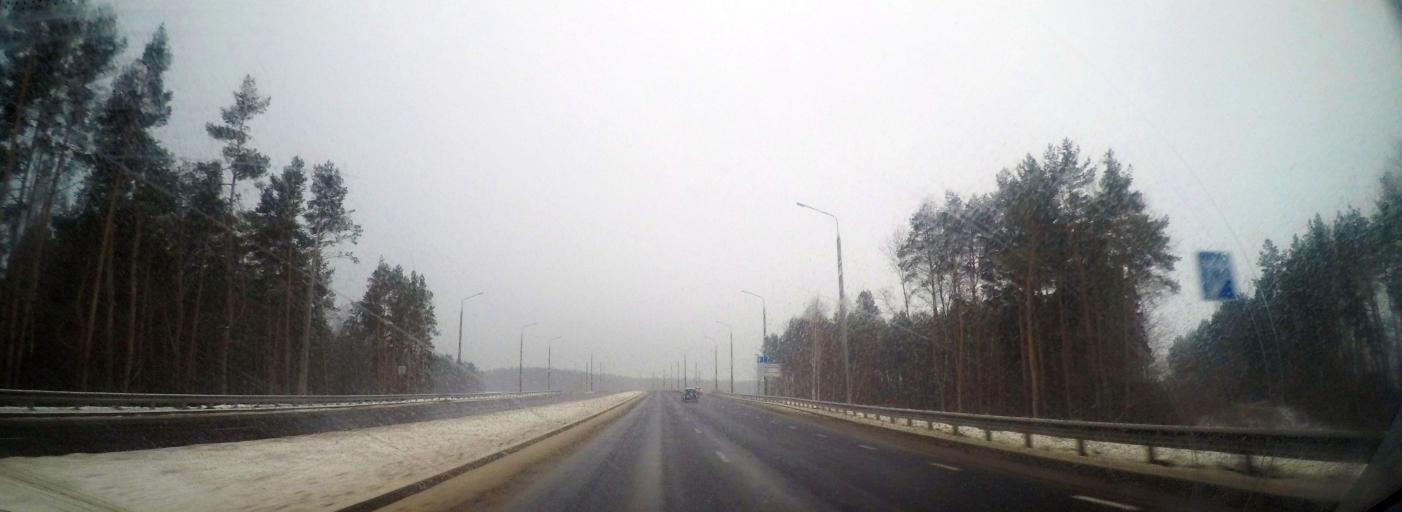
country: BY
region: Grodnenskaya
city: Hrodna
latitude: 53.6411
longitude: 23.8817
